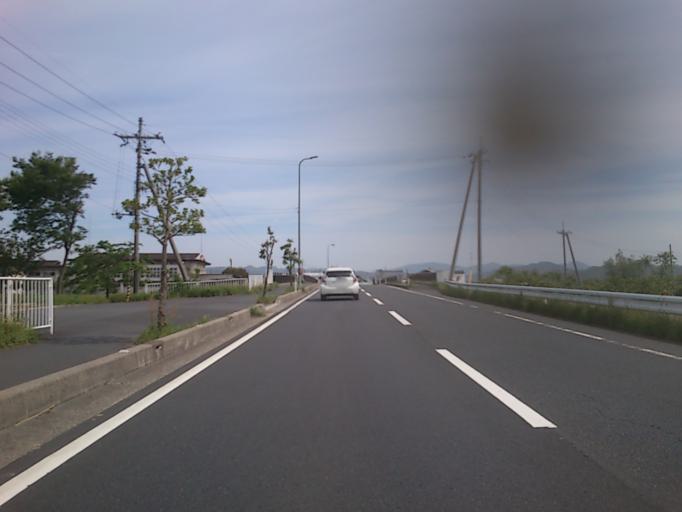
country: JP
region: Kyoto
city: Miyazu
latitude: 35.6156
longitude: 135.0775
